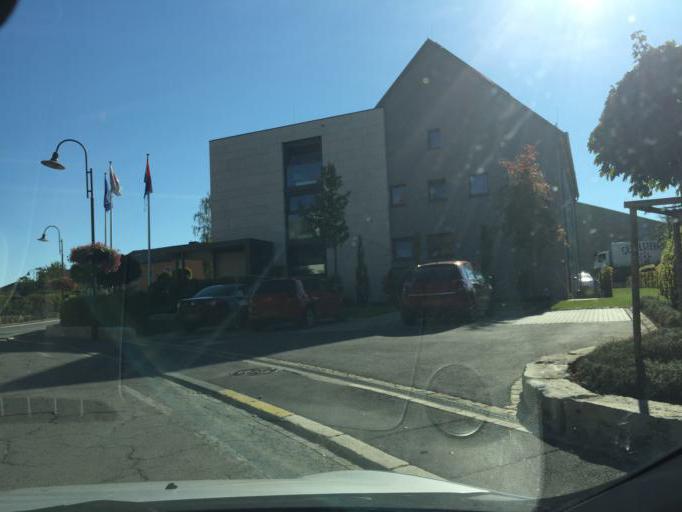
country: LU
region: Luxembourg
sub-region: Canton de Luxembourg
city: Contern
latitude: 49.5848
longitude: 6.2274
